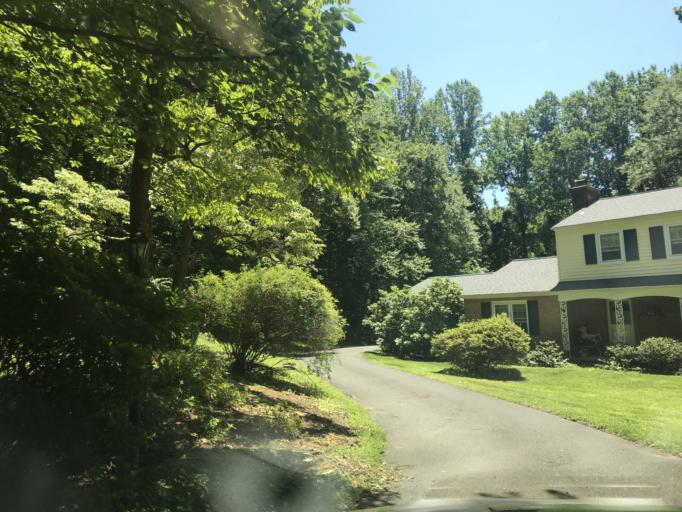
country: US
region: Maryland
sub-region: Baltimore County
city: Kingsville
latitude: 39.4729
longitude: -76.4548
